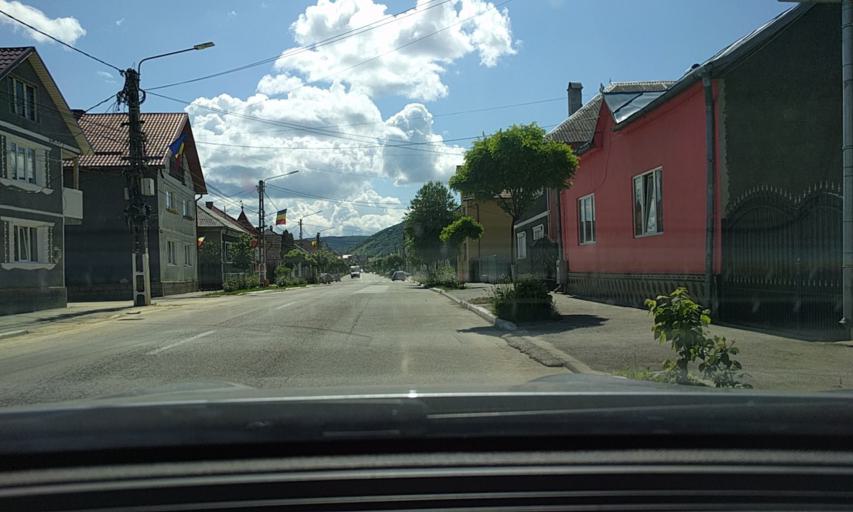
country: RO
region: Bistrita-Nasaud
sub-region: Oras Nasaud
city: Nasaud
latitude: 47.2894
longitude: 24.3920
